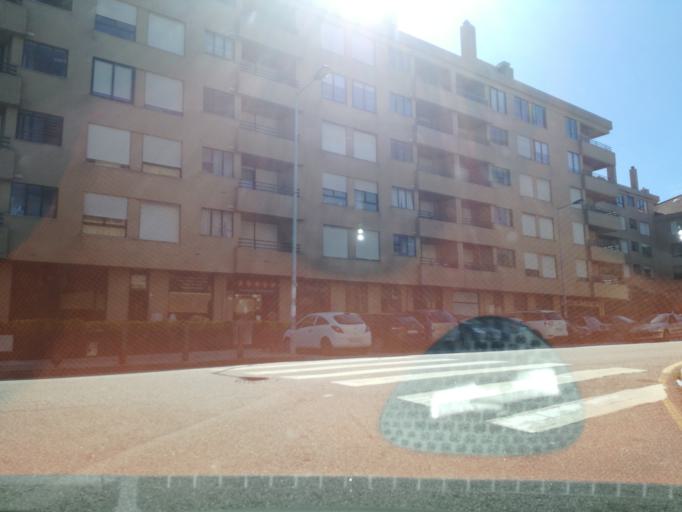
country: PT
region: Porto
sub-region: Matosinhos
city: Sao Mamede de Infesta
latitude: 41.1845
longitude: -8.6012
